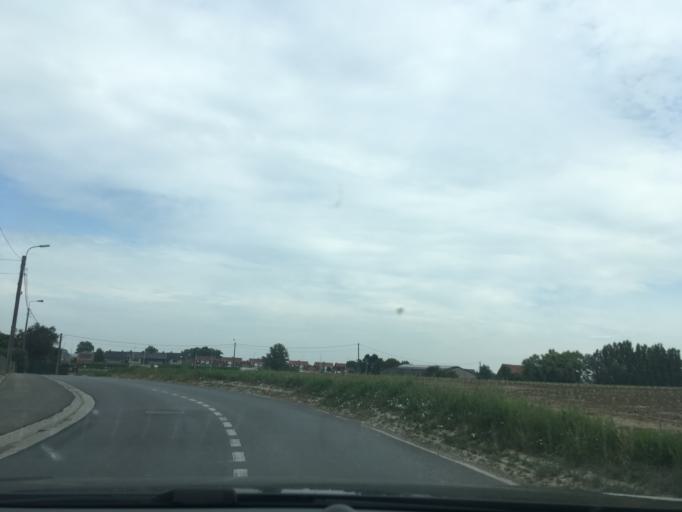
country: BE
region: Flanders
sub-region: Provincie West-Vlaanderen
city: Pittem
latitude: 50.9889
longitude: 3.2809
